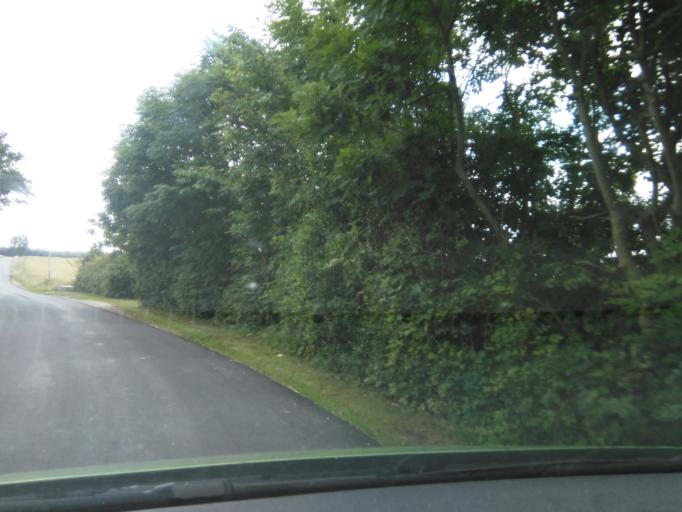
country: DK
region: Central Jutland
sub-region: Arhus Kommune
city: Solbjerg
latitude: 56.0060
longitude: 10.0554
